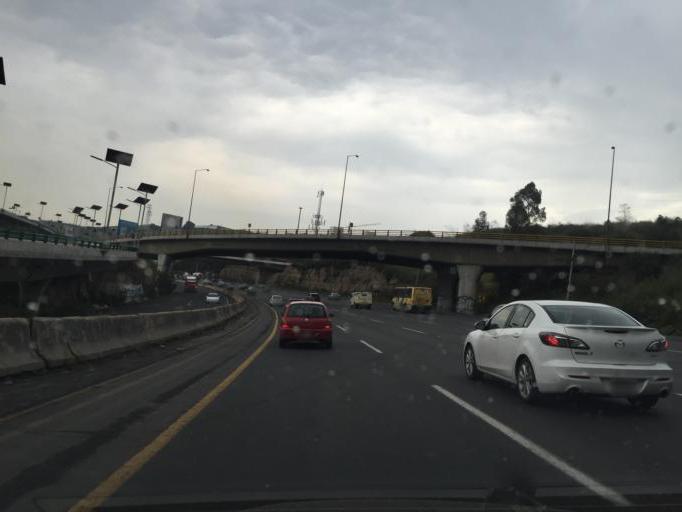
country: MX
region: Mexico
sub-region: Tultitlan
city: Buenavista
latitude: 19.5979
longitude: -99.2000
